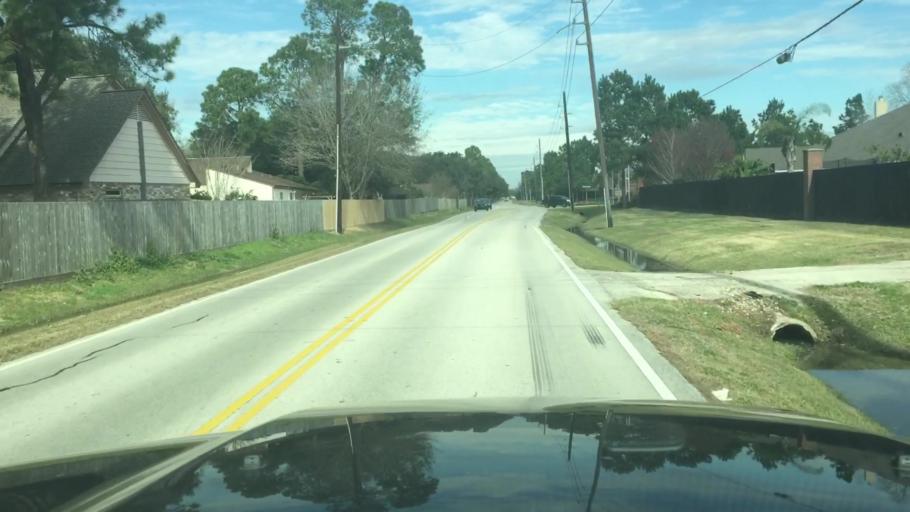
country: US
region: Texas
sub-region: Harris County
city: Oak Cliff Place
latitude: 29.8390
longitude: -95.6752
